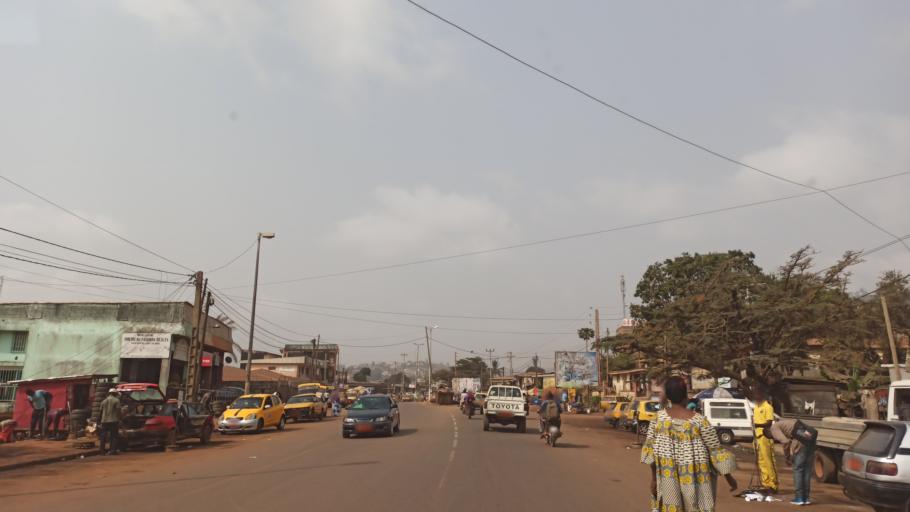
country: CM
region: Centre
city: Yaounde
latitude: 3.8835
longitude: 11.4940
